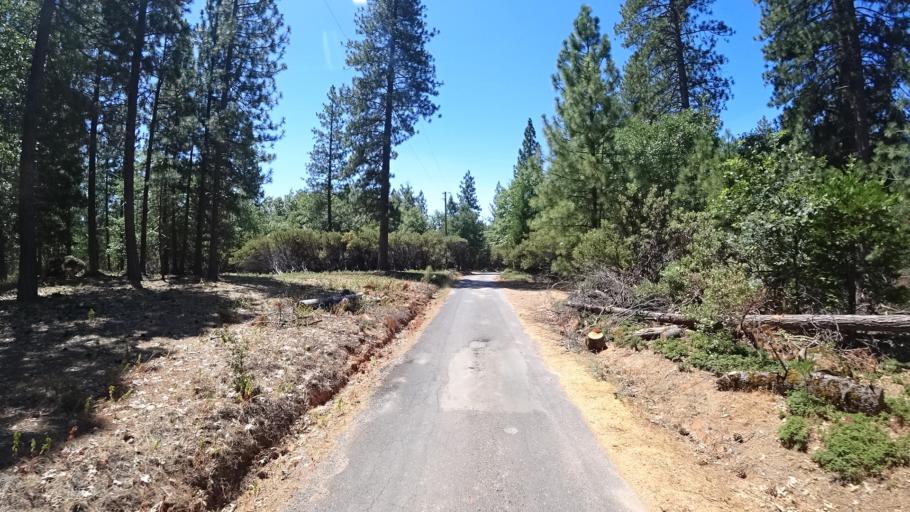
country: US
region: California
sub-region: Amador County
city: Pioneer
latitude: 38.4177
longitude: -120.5018
